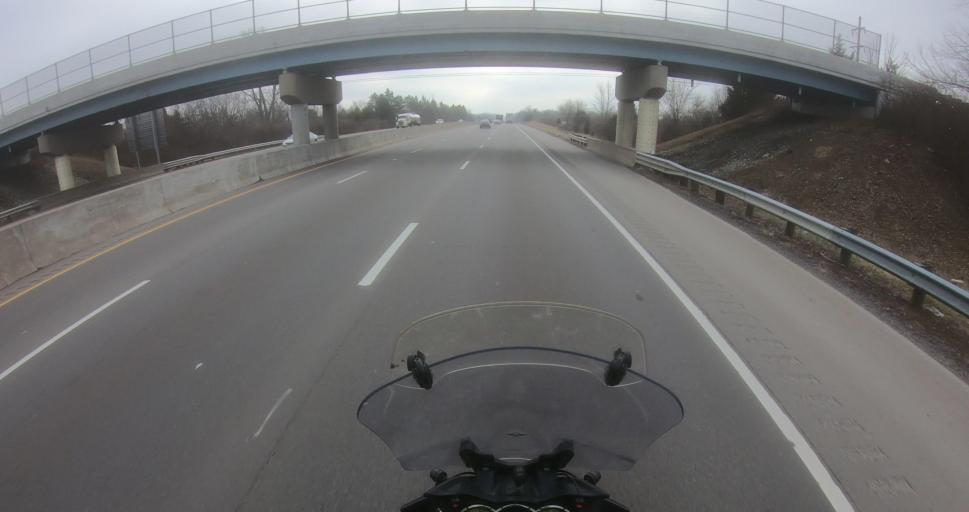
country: US
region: Ohio
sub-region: Miami County
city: Tipp City
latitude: 39.9383
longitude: -84.1895
